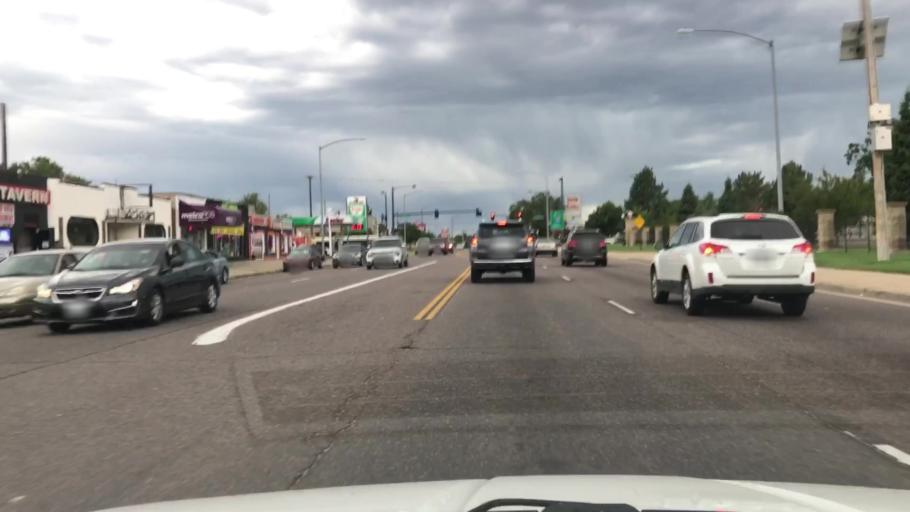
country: US
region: Colorado
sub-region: Adams County
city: Berkley
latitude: 39.7888
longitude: -105.0253
